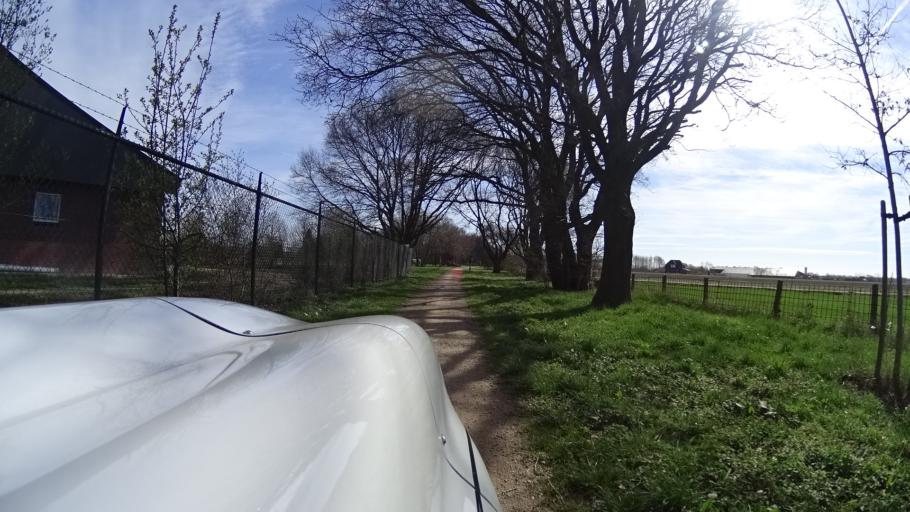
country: NL
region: Limburg
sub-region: Gemeente Gennep
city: Gennep
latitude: 51.6880
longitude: 6.0228
